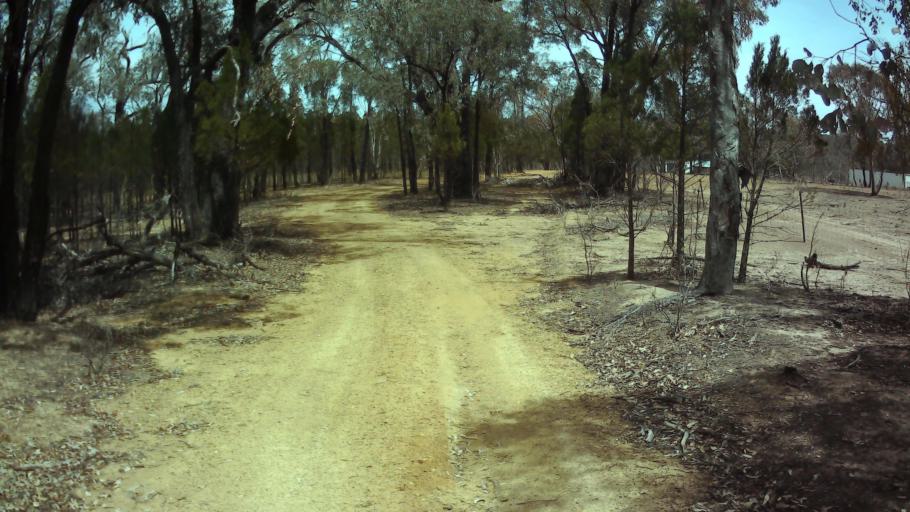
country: AU
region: New South Wales
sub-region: Weddin
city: Grenfell
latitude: -33.8847
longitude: 148.3808
